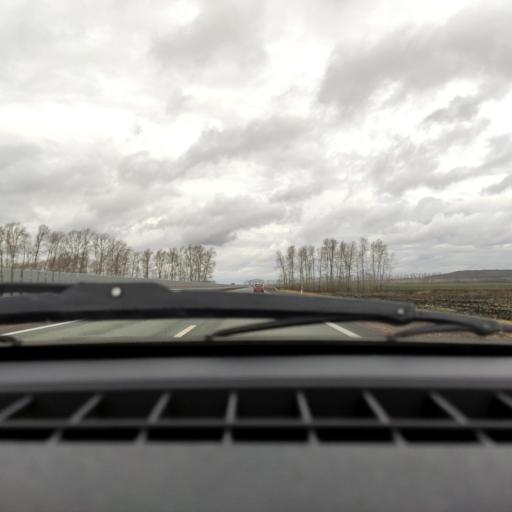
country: RU
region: Bashkortostan
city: Asanovo
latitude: 54.9466
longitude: 55.5826
